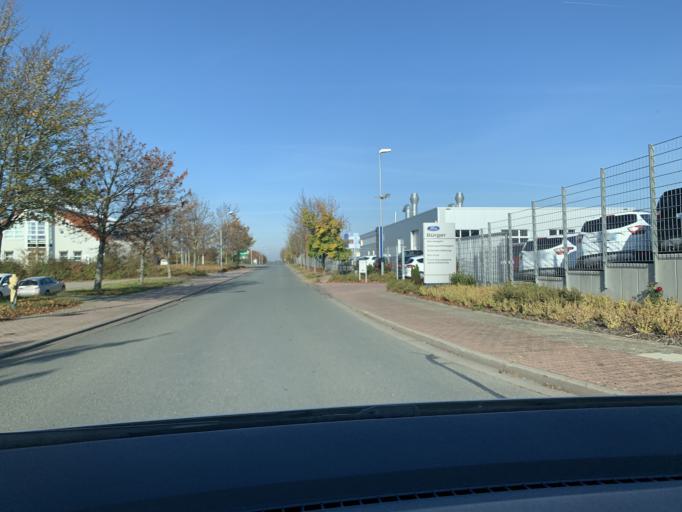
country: DE
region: Thuringia
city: Schmolln
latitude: 50.8823
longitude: 12.3501
